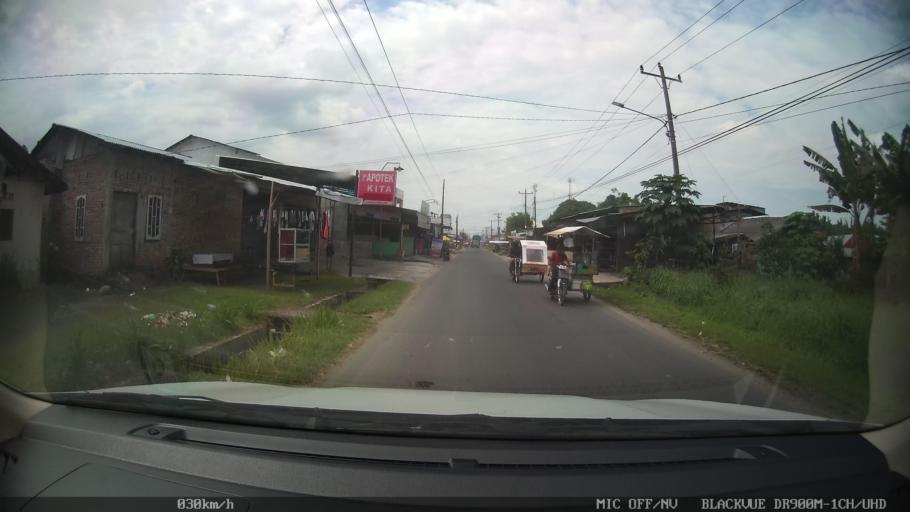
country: ID
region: North Sumatra
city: Sunggal
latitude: 3.6286
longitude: 98.5938
